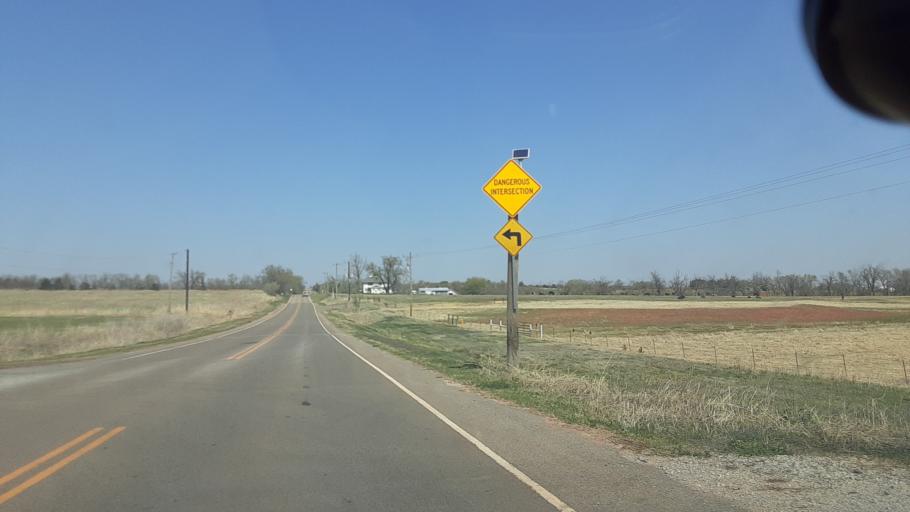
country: US
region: Oklahoma
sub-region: Logan County
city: Guthrie
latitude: 35.8144
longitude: -97.4783
